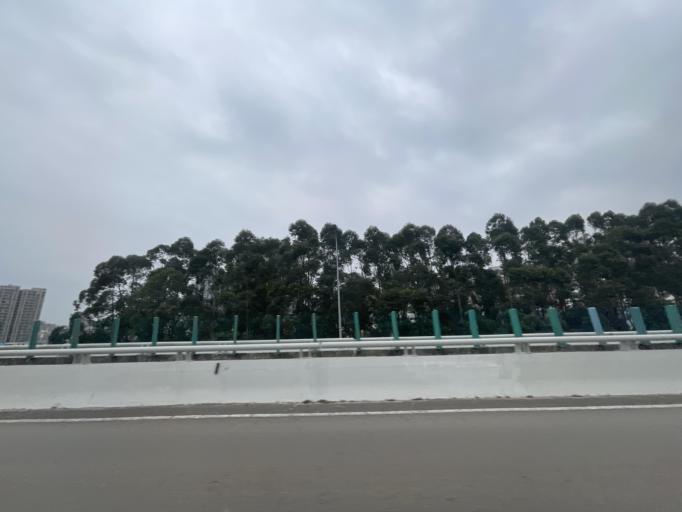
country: CN
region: Guangdong
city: Humen
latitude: 22.8061
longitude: 113.6744
